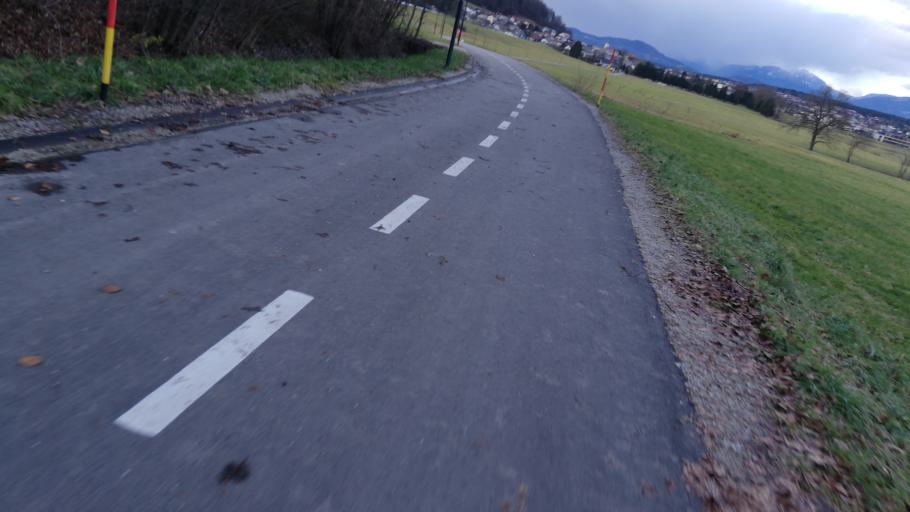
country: SI
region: Medvode
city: Medvode
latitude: 46.1242
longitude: 14.4196
